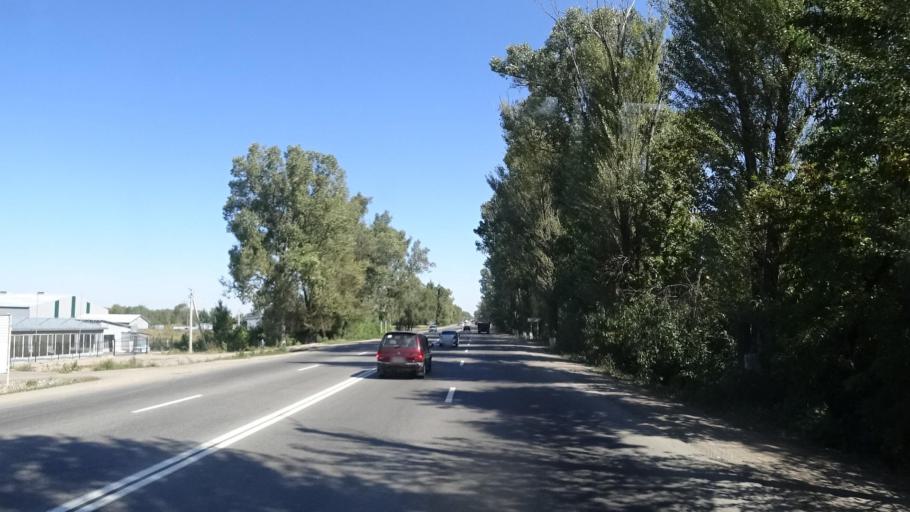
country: KZ
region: Almaty Oblysy
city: Energeticheskiy
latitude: 43.3621
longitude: 77.0800
